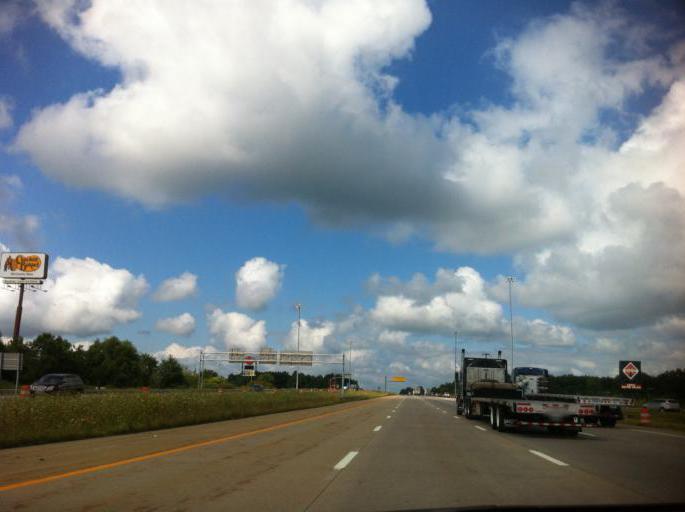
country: US
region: Ohio
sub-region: Trumbull County
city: Mineral Ridge
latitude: 41.1239
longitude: -80.7702
